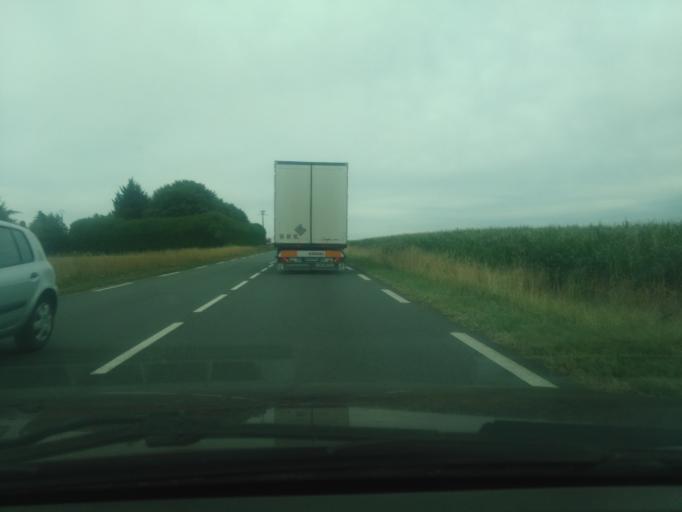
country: FR
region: Poitou-Charentes
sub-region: Departement de la Vienne
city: Bonnes
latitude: 46.5637
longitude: 0.5748
